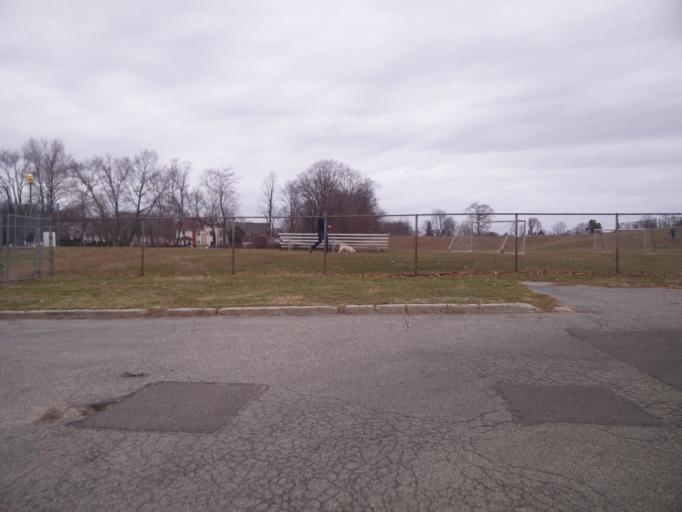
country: US
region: New York
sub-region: Nassau County
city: Glen Cove
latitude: 40.8718
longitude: -73.6295
